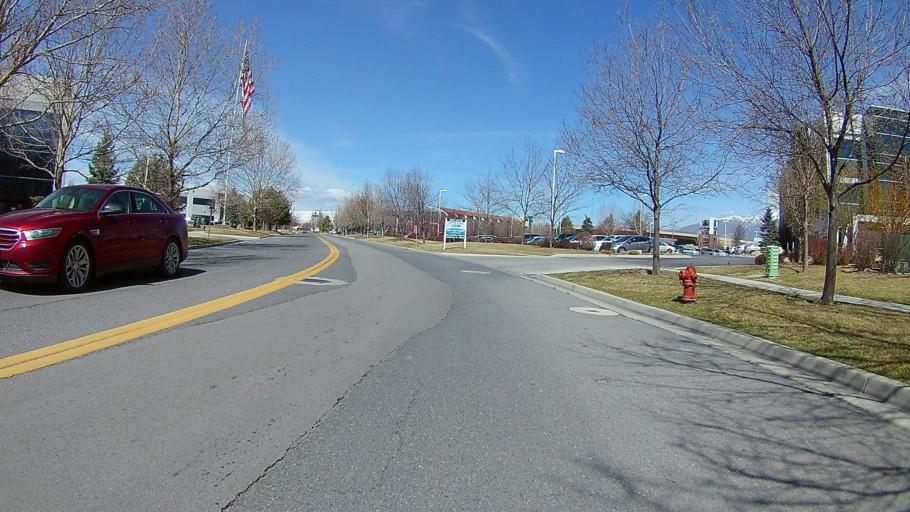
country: US
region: Utah
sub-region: Utah County
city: American Fork
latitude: 40.3523
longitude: -111.7761
